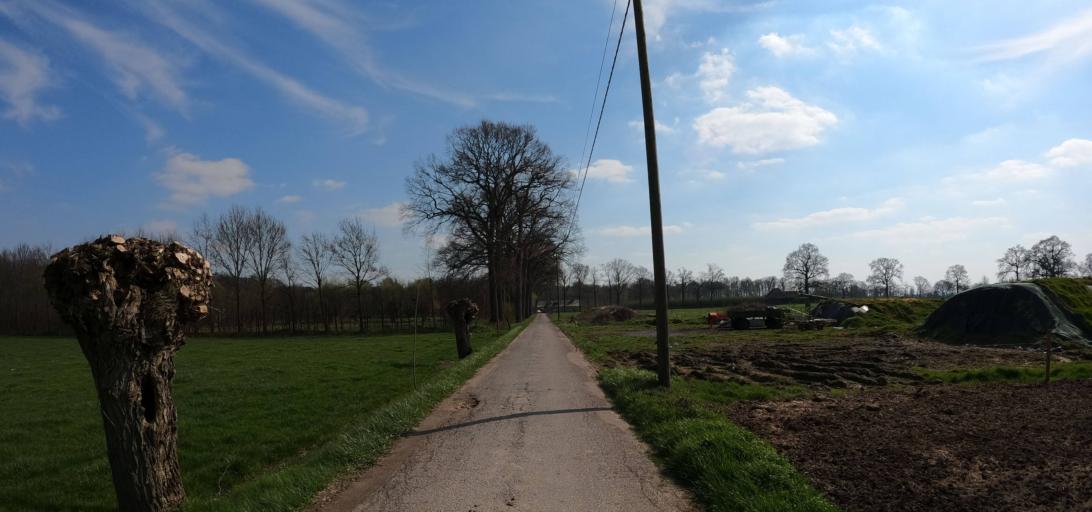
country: BE
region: Flanders
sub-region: Provincie Antwerpen
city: Aartselaar
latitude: 51.1354
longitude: 4.4124
